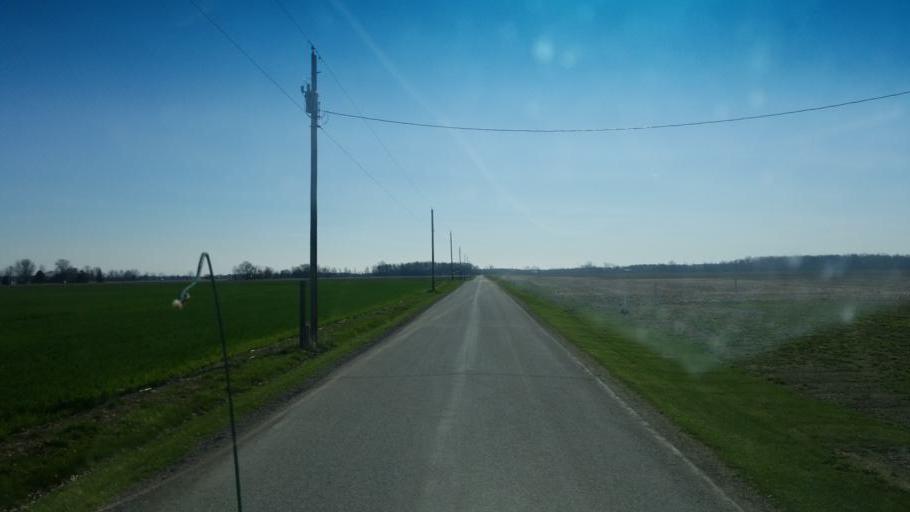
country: US
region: Ohio
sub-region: Hardin County
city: Forest
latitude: 40.7018
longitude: -83.5212
